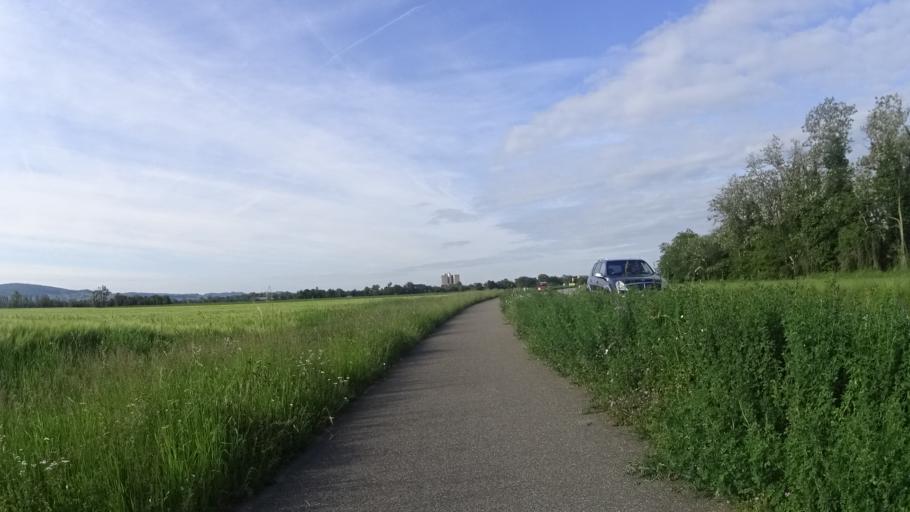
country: DE
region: Baden-Wuerttemberg
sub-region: Freiburg Region
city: Neuenburg am Rhein
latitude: 47.8243
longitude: 7.5742
